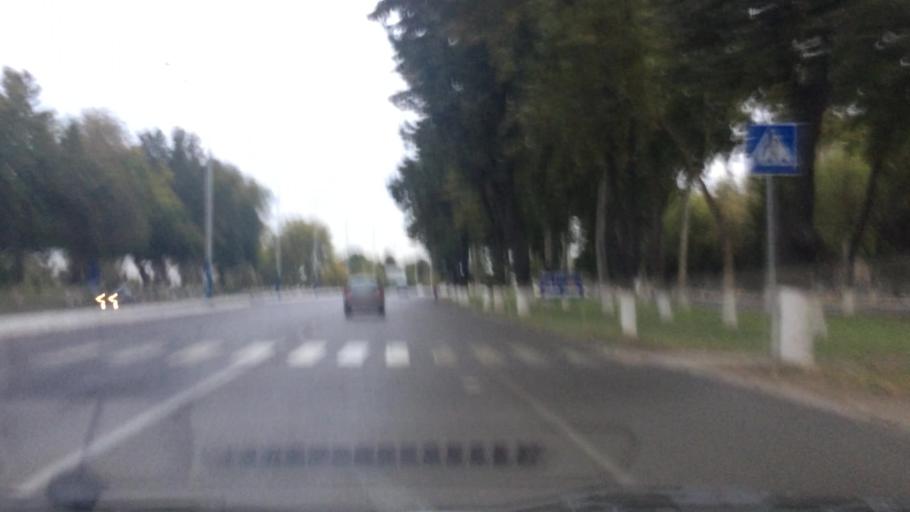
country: UZ
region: Toshkent Shahri
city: Tashkent
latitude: 41.2601
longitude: 69.1963
